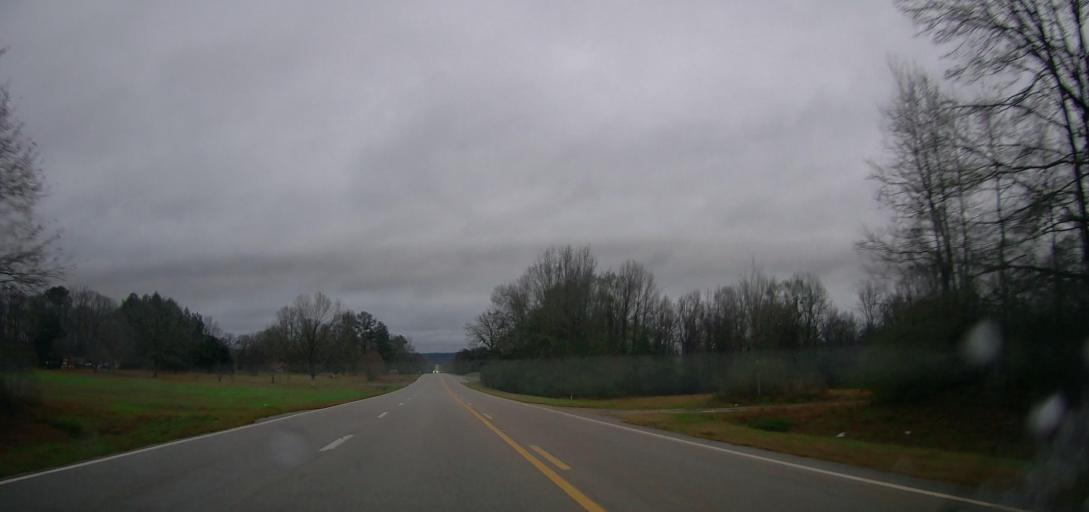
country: US
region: Alabama
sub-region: Bibb County
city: Centreville
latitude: 32.8582
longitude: -86.9662
